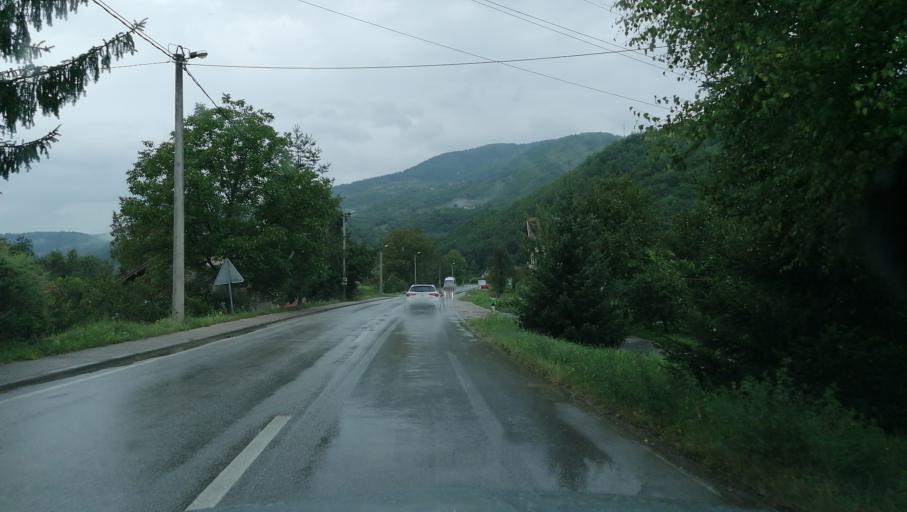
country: BA
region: Federation of Bosnia and Herzegovina
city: Gorazde
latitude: 43.6820
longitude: 19.0073
